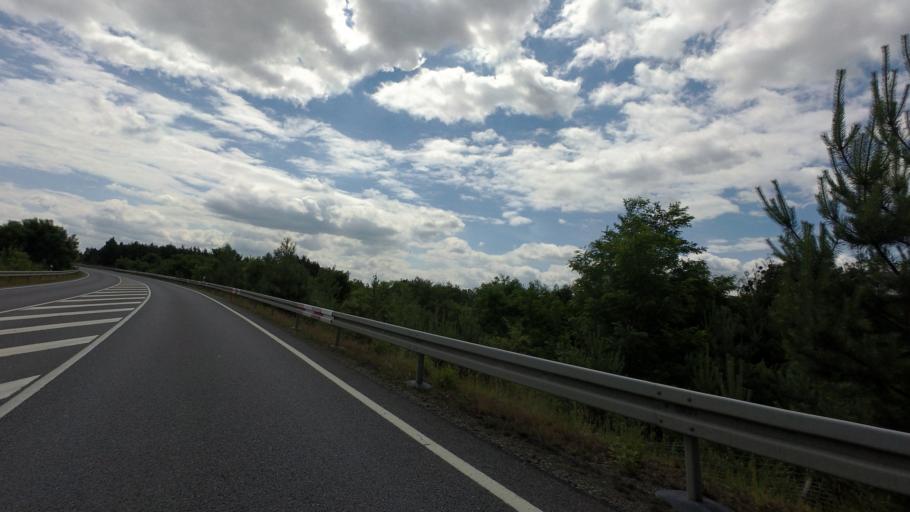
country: DE
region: Brandenburg
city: Senftenberg
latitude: 51.5337
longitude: 14.0235
